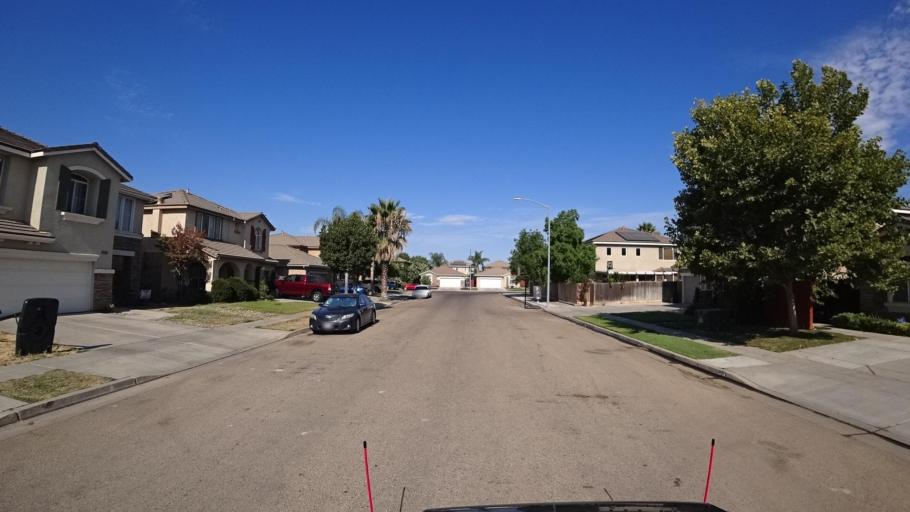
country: US
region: California
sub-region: Fresno County
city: Tarpey Village
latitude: 36.7823
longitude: -119.6606
